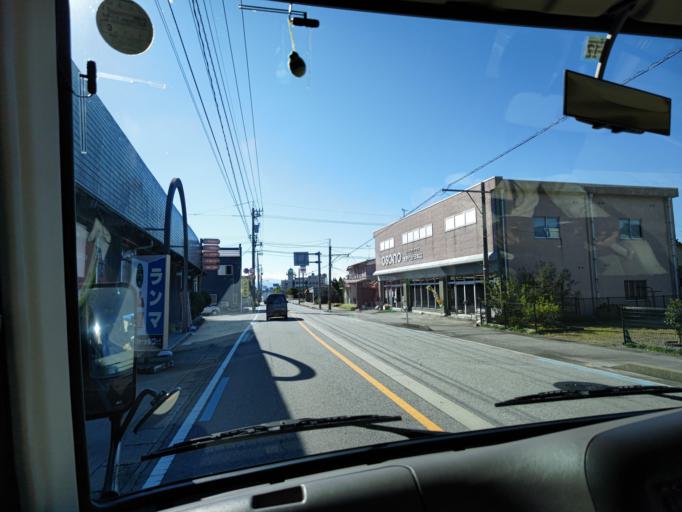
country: JP
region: Toyama
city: Nyuzen
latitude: 36.8949
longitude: 137.4194
